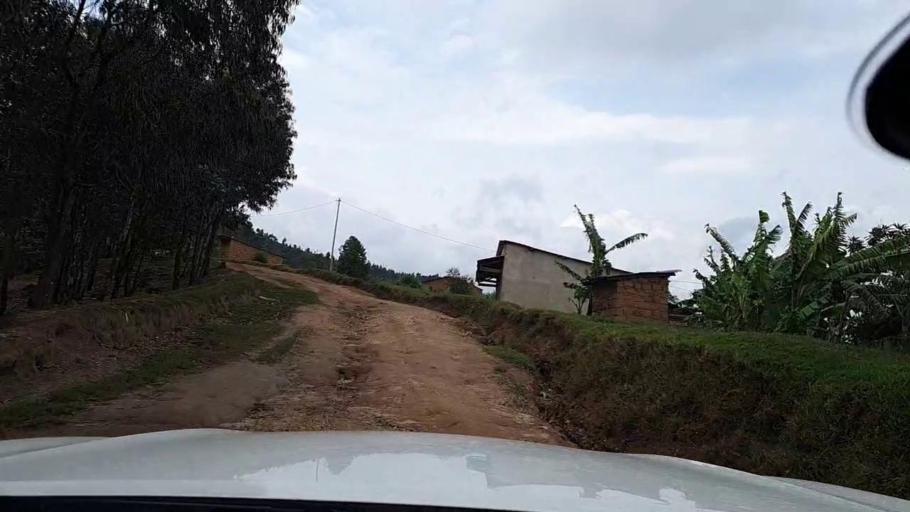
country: RW
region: Western Province
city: Kibuye
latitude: -2.1988
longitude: 29.3202
